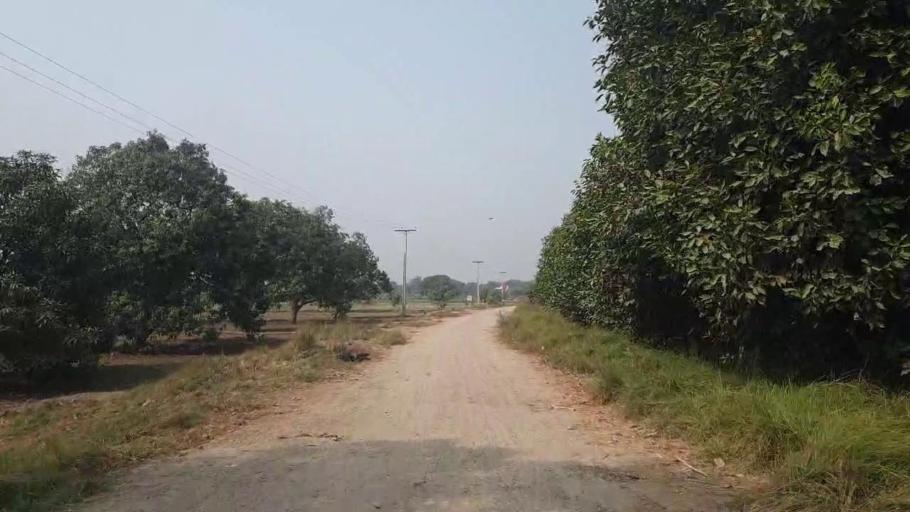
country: PK
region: Sindh
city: Tando Muhammad Khan
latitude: 25.2697
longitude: 68.5810
